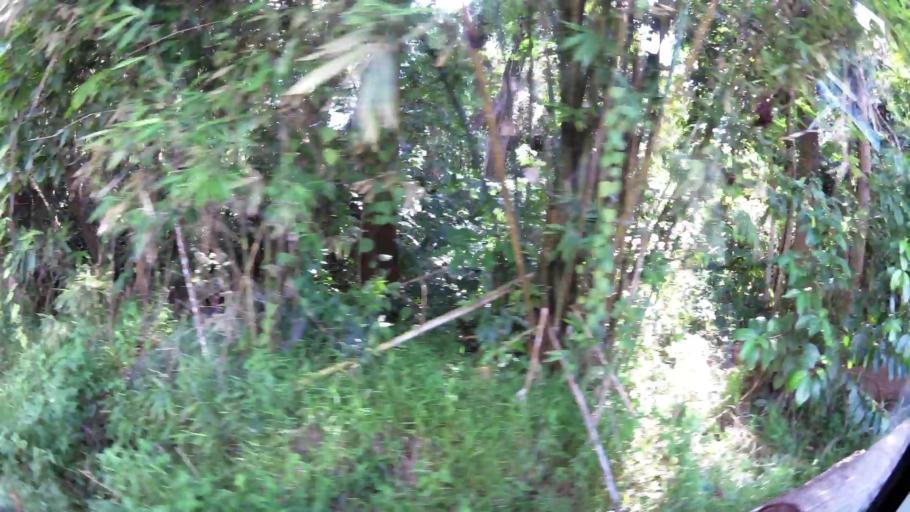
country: BN
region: Brunei and Muara
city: Bandar Seri Begawan
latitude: 5.0286
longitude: 115.0487
